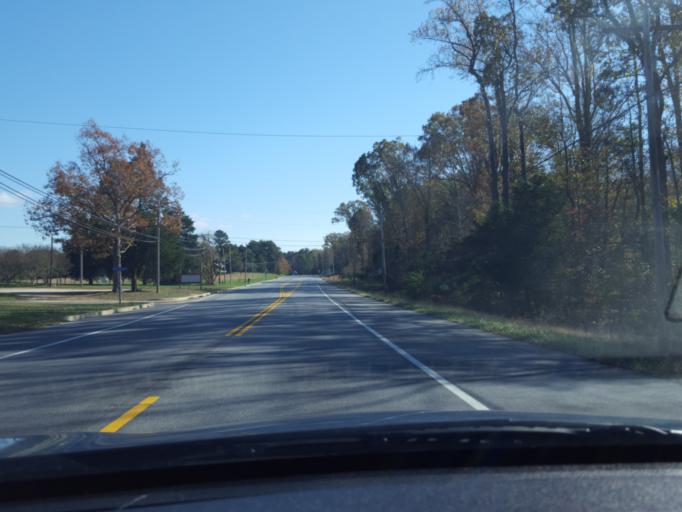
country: US
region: Maryland
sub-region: Saint Mary's County
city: Leonardtown
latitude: 38.2528
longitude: -76.5953
